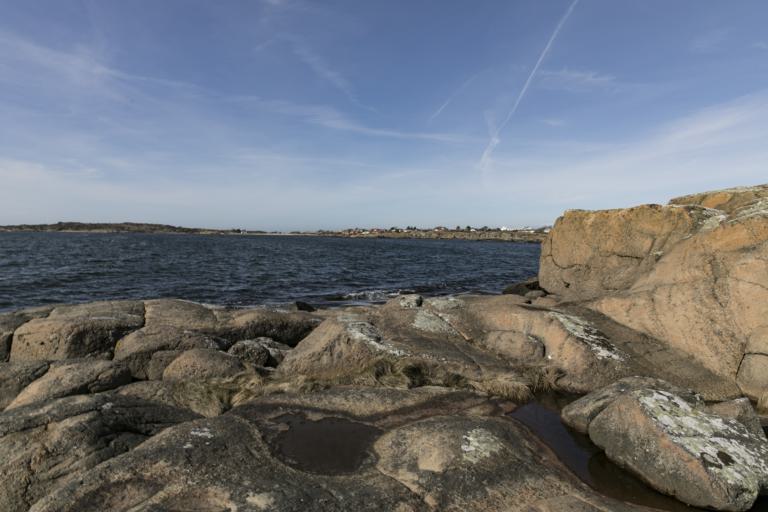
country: SE
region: Halland
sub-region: Varbergs Kommun
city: Varberg
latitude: 57.1103
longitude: 12.2126
